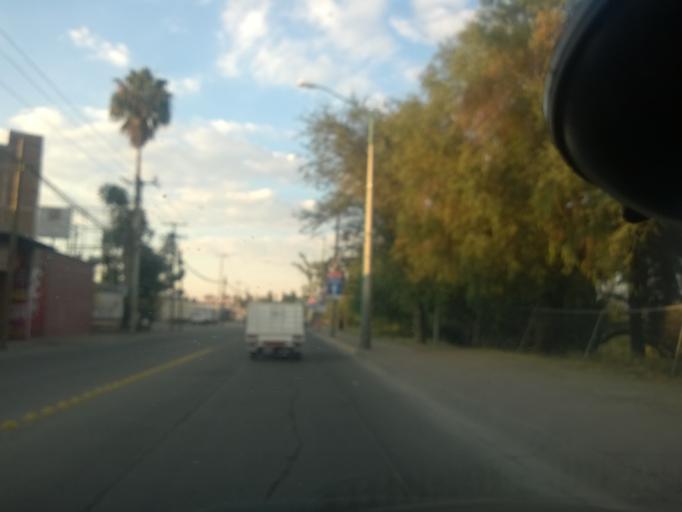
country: MX
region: Guanajuato
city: Leon
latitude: 21.1674
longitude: -101.6854
